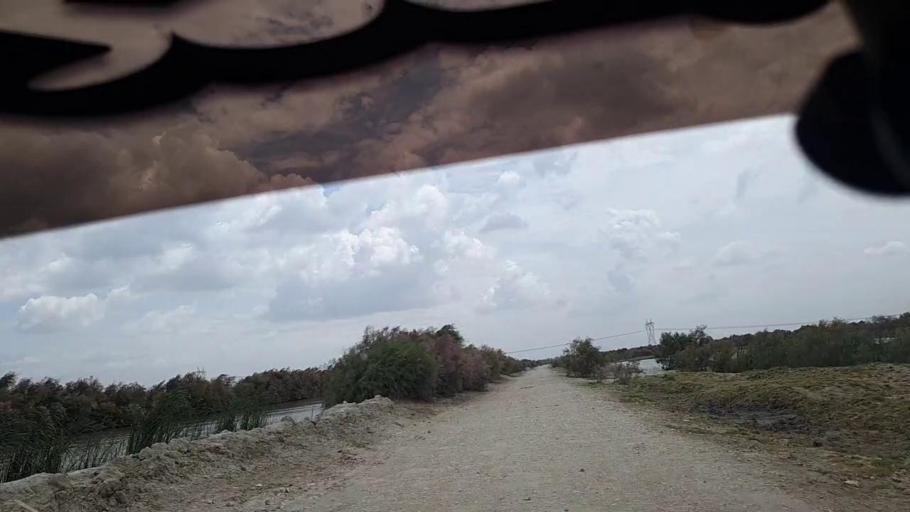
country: PK
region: Sindh
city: Ghauspur
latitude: 28.0702
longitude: 68.9372
